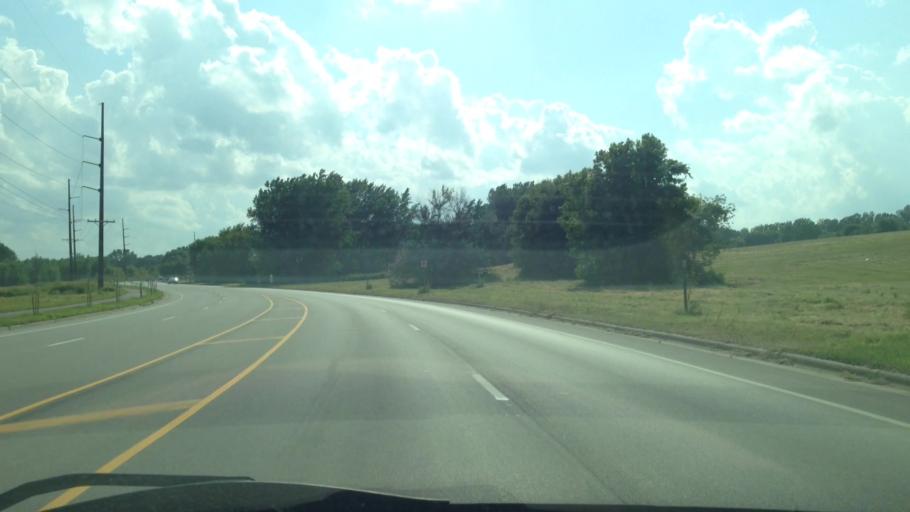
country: US
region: Minnesota
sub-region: Olmsted County
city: Rochester
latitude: 44.0652
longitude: -92.5128
